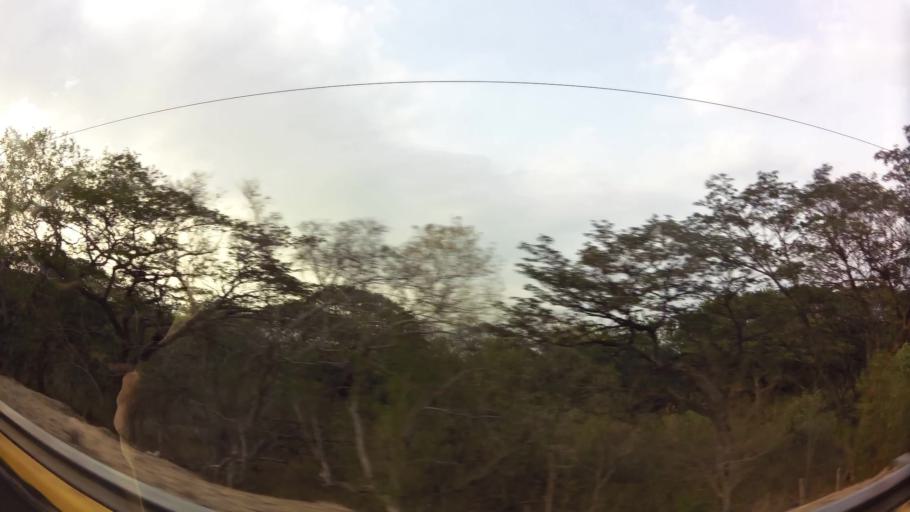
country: NI
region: Leon
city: Nagarote
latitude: 12.2617
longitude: -86.4668
